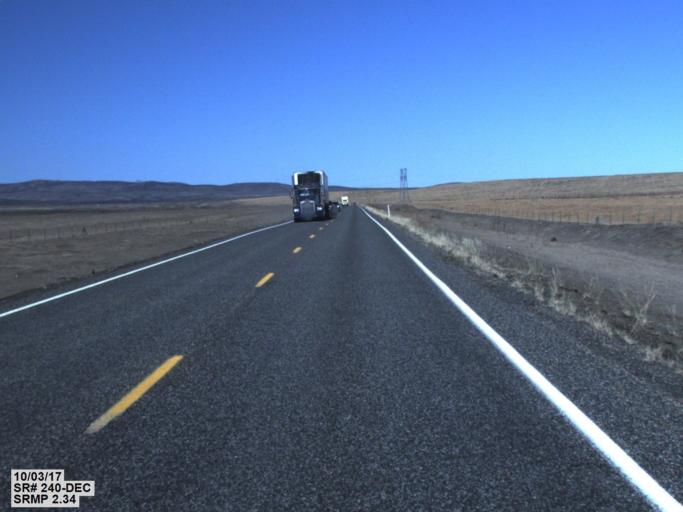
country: US
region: Washington
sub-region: Grant County
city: Desert Aire
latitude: 46.5526
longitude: -119.6980
